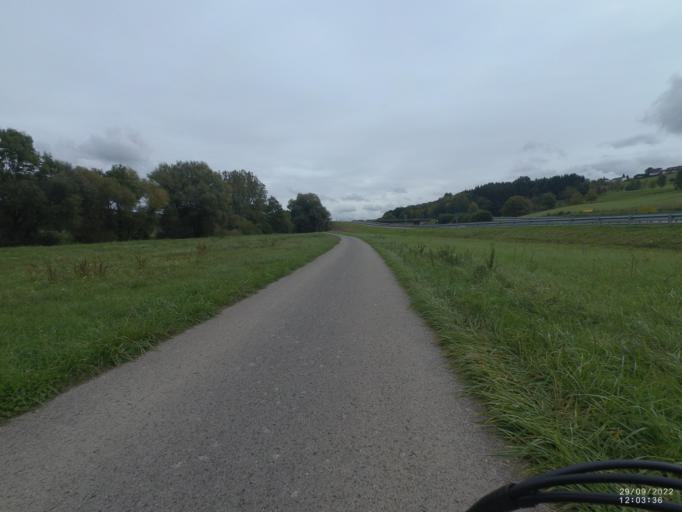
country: DE
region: Baden-Wuerttemberg
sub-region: Regierungsbezirk Stuttgart
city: Ebersbach an der Fils
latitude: 48.7118
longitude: 9.5024
